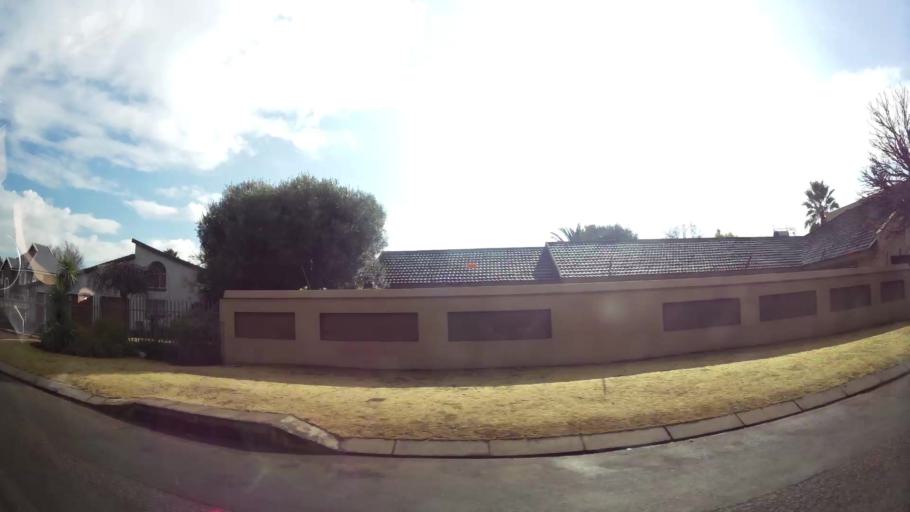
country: ZA
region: Gauteng
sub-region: Sedibeng District Municipality
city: Meyerton
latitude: -26.5512
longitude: 28.0301
